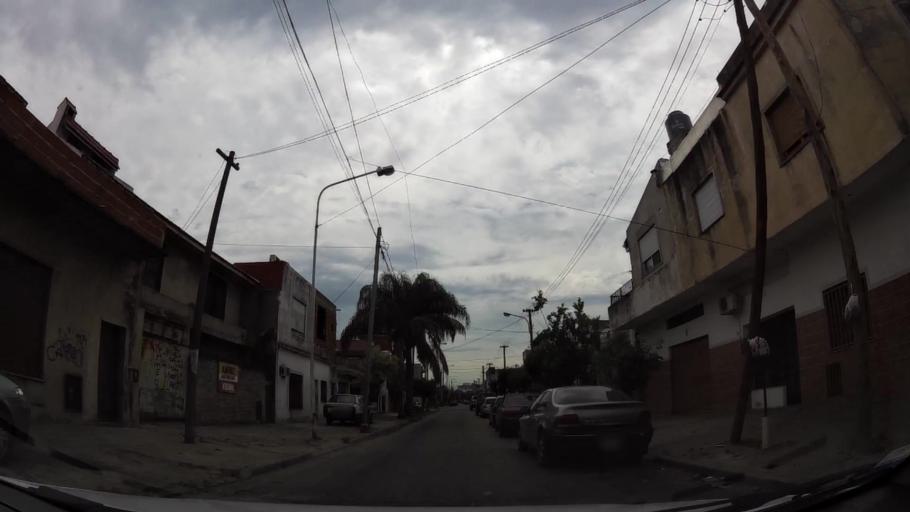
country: AR
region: Buenos Aires F.D.
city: Villa Lugano
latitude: -34.6840
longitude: -58.5098
